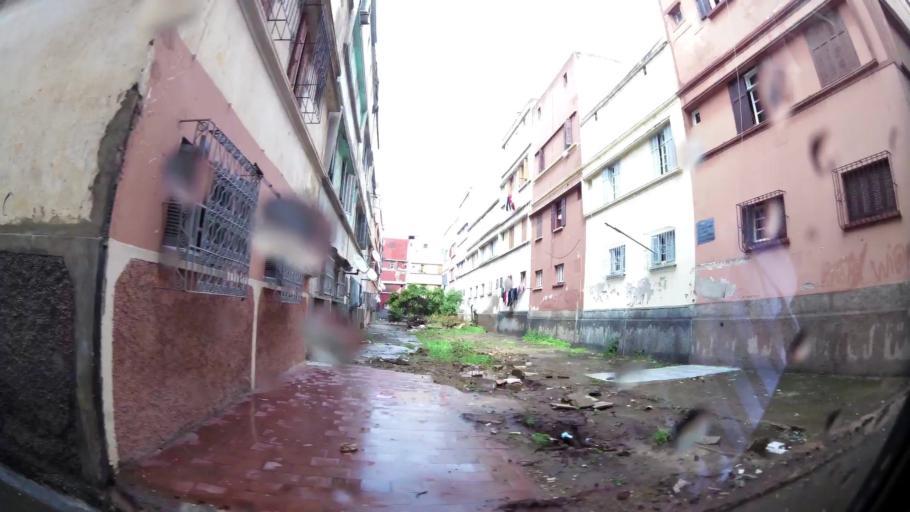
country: MA
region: Grand Casablanca
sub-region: Casablanca
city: Casablanca
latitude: 33.5445
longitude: -7.5734
